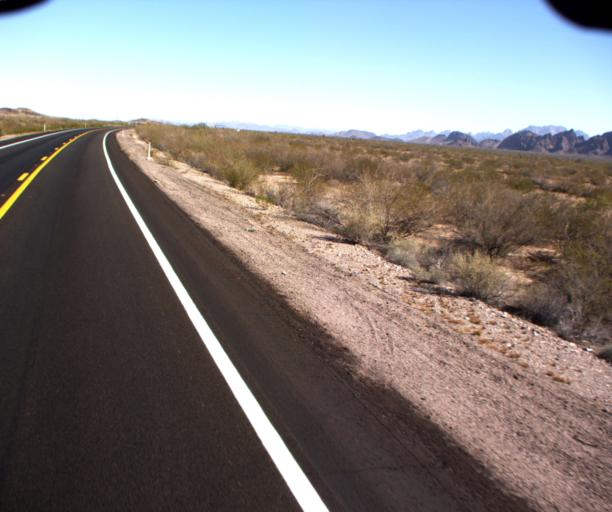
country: US
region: Arizona
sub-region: La Paz County
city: Quartzsite
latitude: 33.2522
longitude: -114.2468
